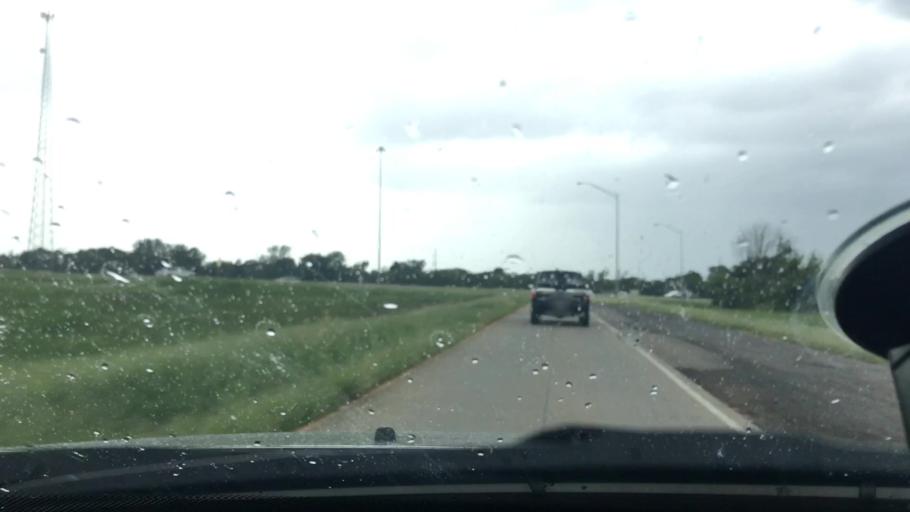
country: US
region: Oklahoma
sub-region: Okmulgee County
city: Henryetta
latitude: 35.4337
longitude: -95.9733
